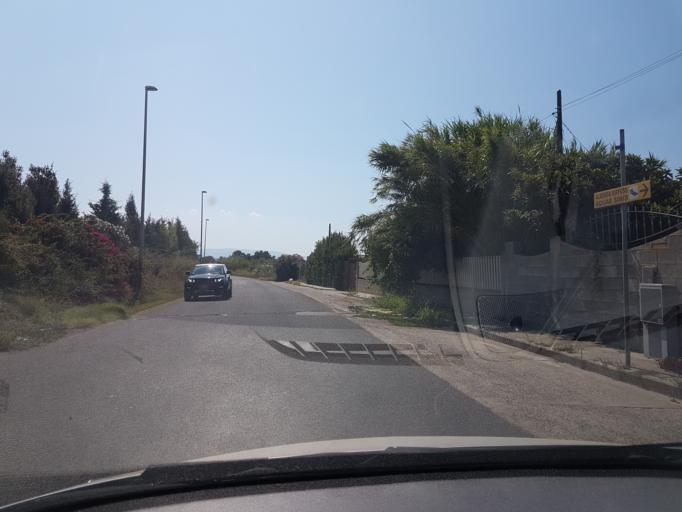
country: IT
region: Sardinia
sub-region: Provincia di Oristano
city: Solanas
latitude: 39.9274
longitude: 8.5550
